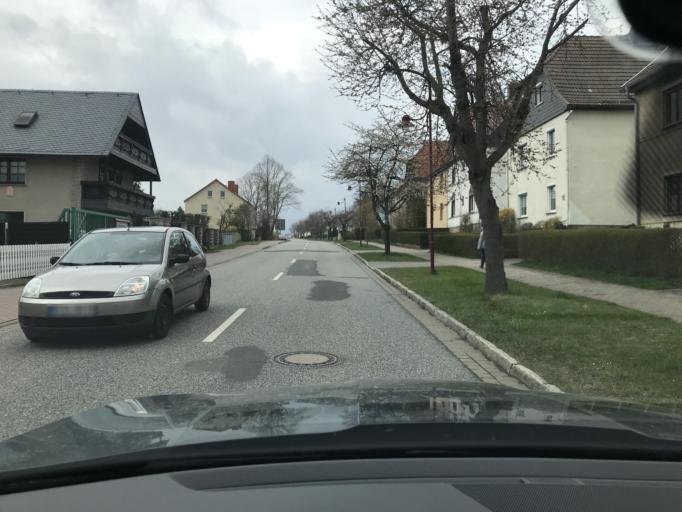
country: DE
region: Saxony-Anhalt
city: Harzgerode
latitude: 51.6470
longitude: 11.1402
